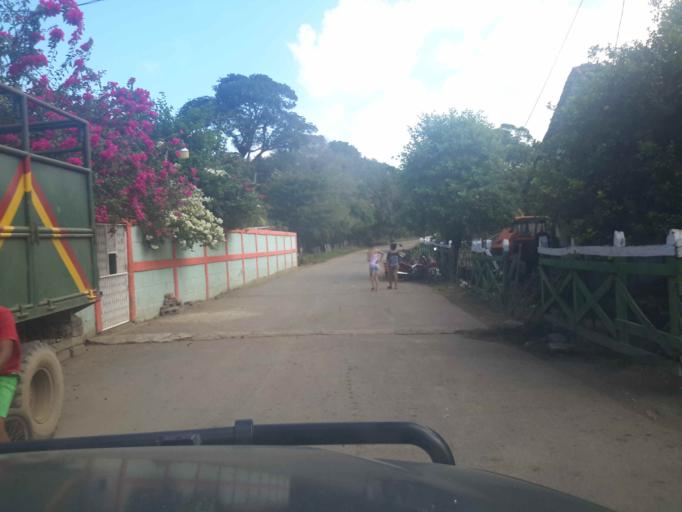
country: NI
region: Granada
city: Nandaime
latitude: 11.6569
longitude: -85.9707
